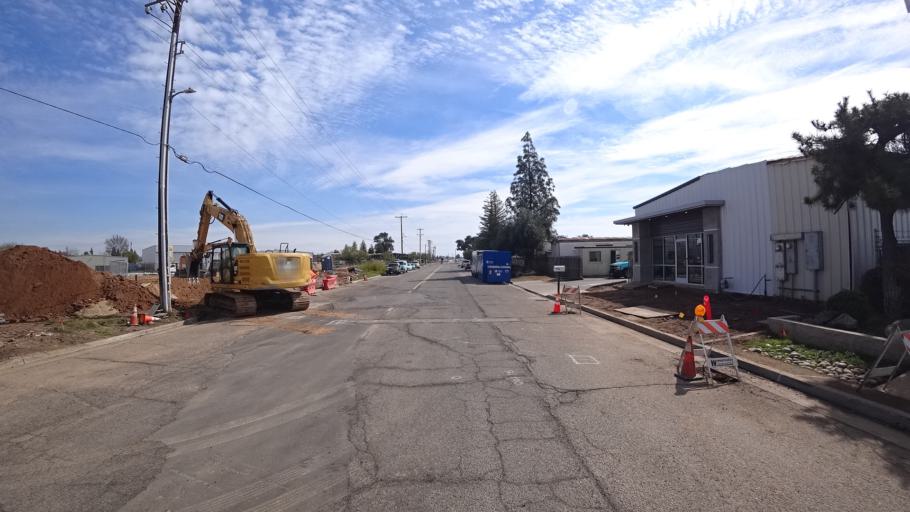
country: US
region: California
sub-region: Fresno County
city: West Park
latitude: 36.8154
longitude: -119.8921
